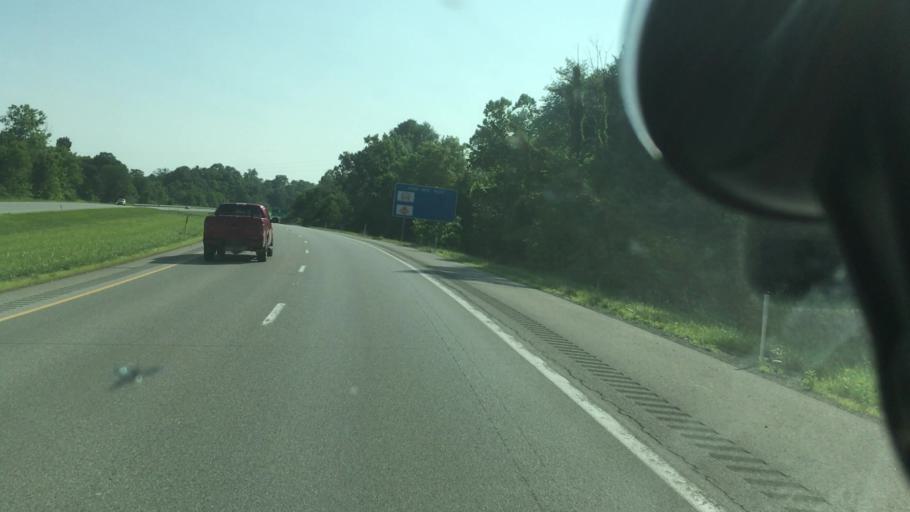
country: US
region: Pennsylvania
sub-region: Lawrence County
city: New Castle
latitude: 40.9686
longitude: -80.3251
